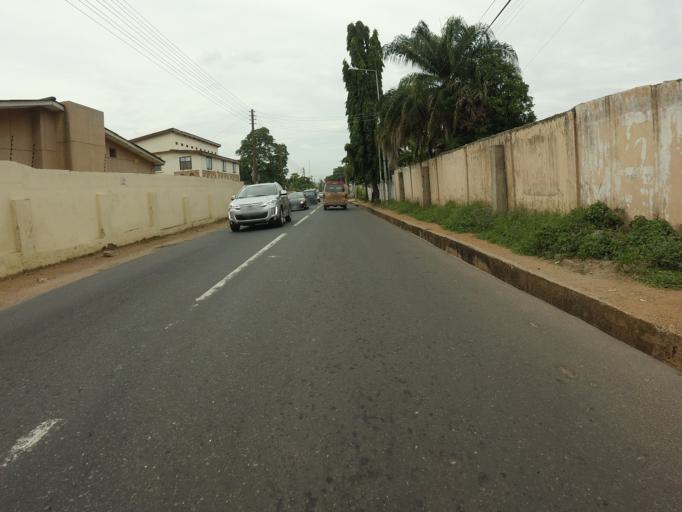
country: GH
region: Greater Accra
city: Dome
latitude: 5.5987
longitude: -0.2286
